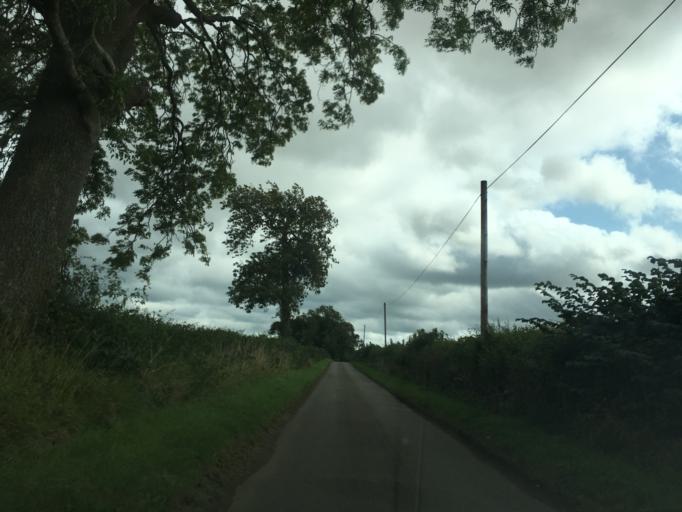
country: GB
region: Scotland
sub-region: Falkirk
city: Bo'ness
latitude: 55.9957
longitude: -3.6359
